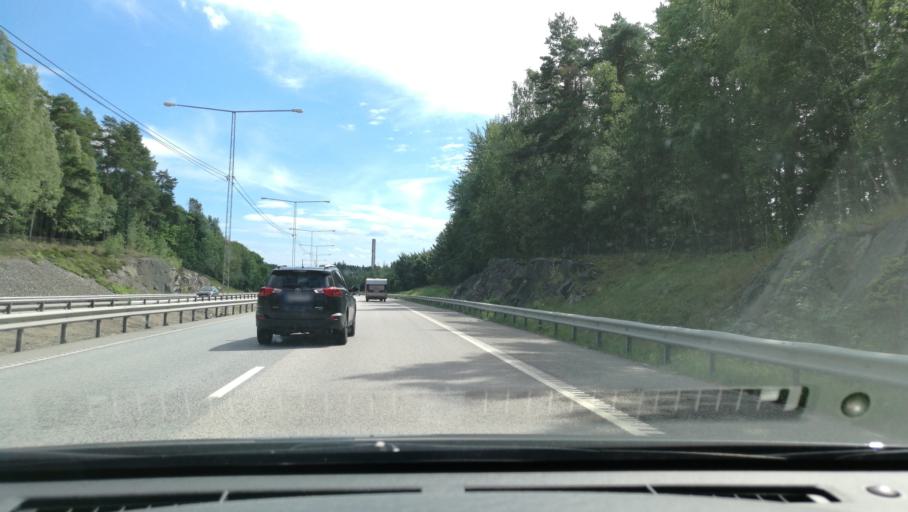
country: SE
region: Stockholm
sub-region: Jarfalla Kommun
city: Jakobsberg
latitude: 59.4361
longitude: 17.8442
